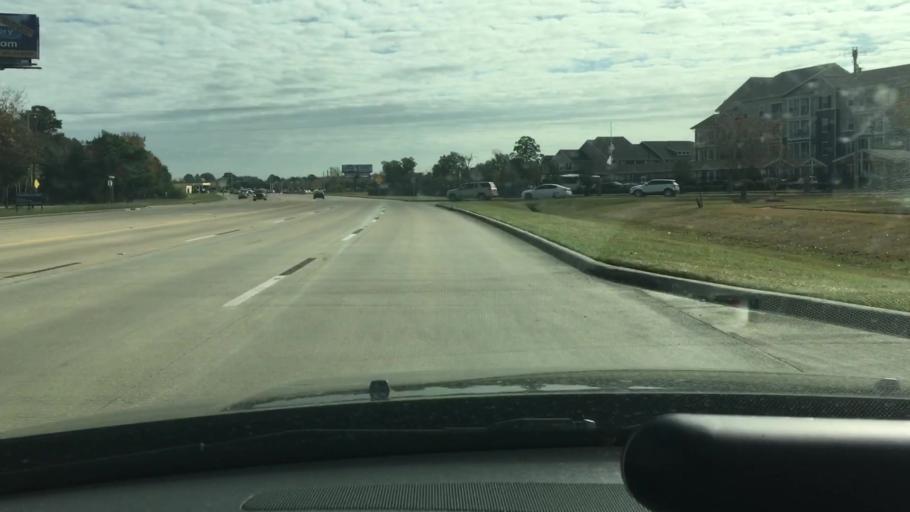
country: US
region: Texas
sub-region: Galveston County
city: League City
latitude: 29.5232
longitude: -95.0826
